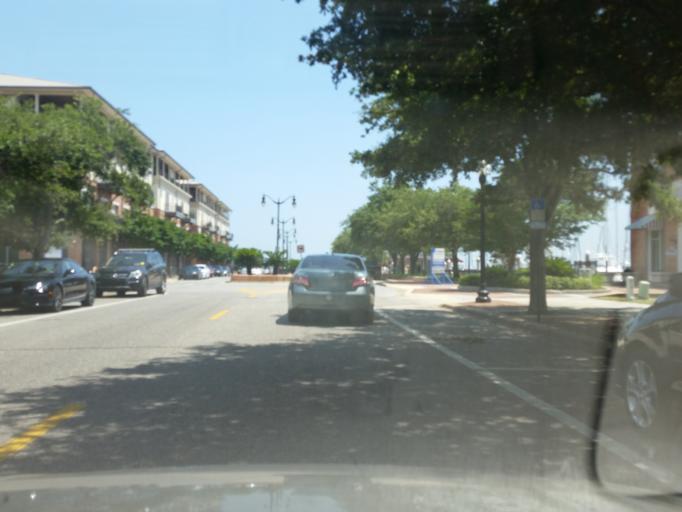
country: US
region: Florida
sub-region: Escambia County
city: Pensacola
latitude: 30.4045
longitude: -87.2135
